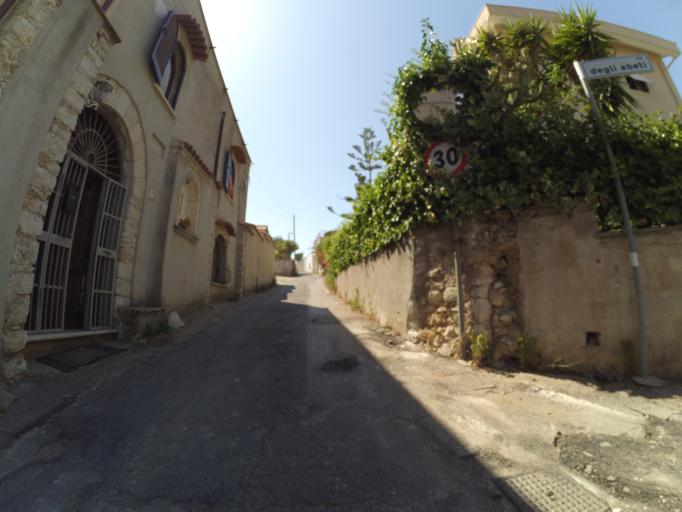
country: IT
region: Latium
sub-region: Provincia di Latina
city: Gaeta
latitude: 41.2182
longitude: 13.5578
